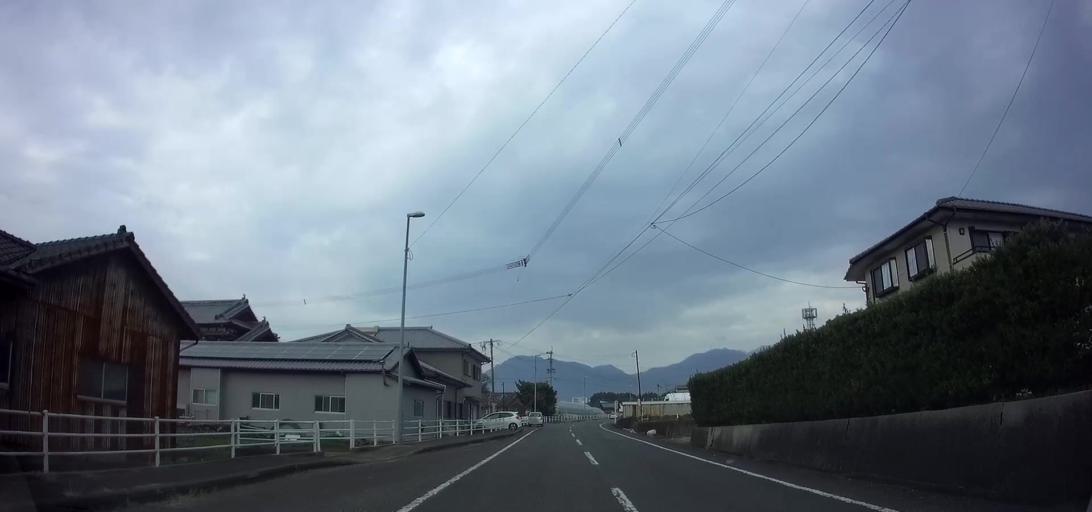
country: JP
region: Nagasaki
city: Shimabara
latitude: 32.6596
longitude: 130.3111
